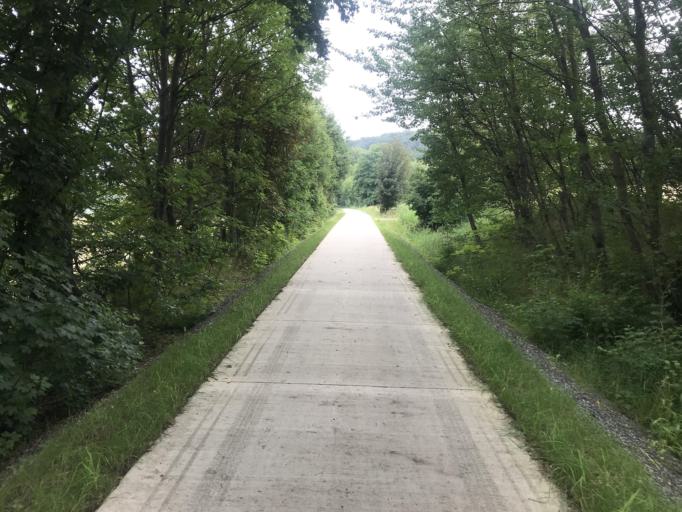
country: DE
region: Saxony-Anhalt
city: Rieder
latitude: 51.7281
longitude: 11.1876
